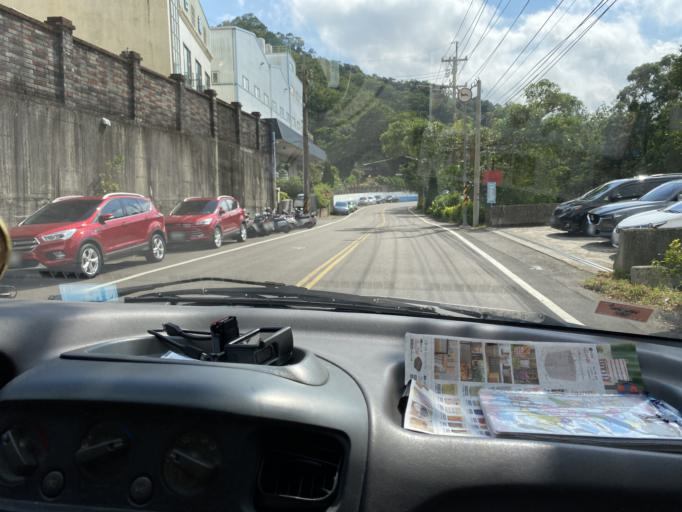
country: TW
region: Taiwan
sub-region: Hsinchu
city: Zhubei
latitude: 24.7426
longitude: 121.1348
